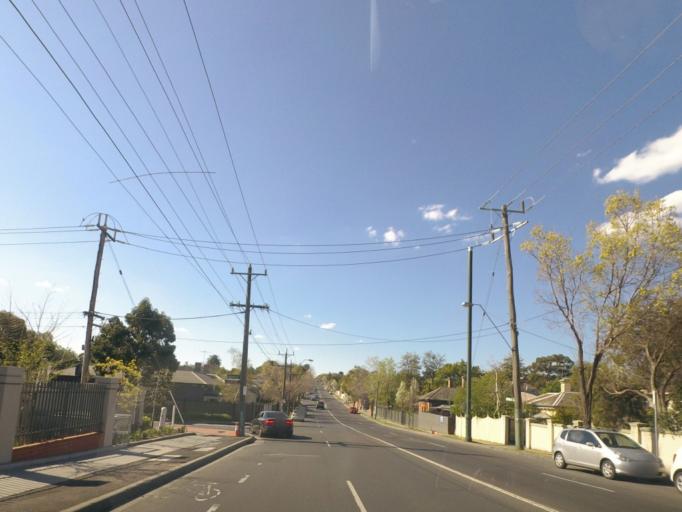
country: AU
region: Victoria
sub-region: Boroondara
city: Kew
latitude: -37.8201
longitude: 145.0266
